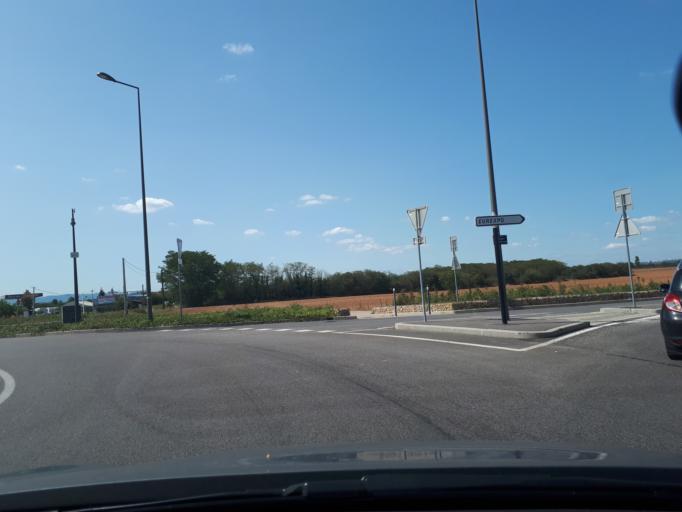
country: FR
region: Rhone-Alpes
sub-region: Departement du Rhone
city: Saint-Priest
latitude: 45.7183
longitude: 4.9548
